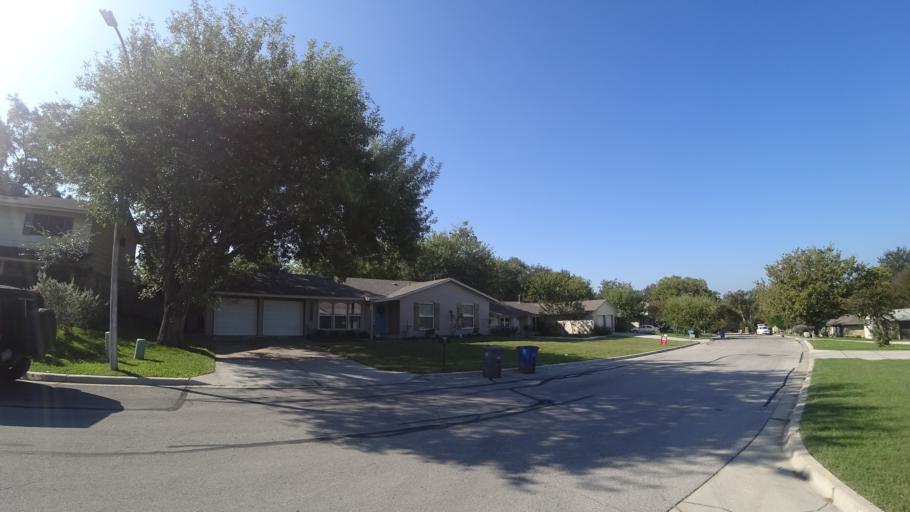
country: US
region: Texas
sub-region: Travis County
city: Austin
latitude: 30.3208
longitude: -97.6696
